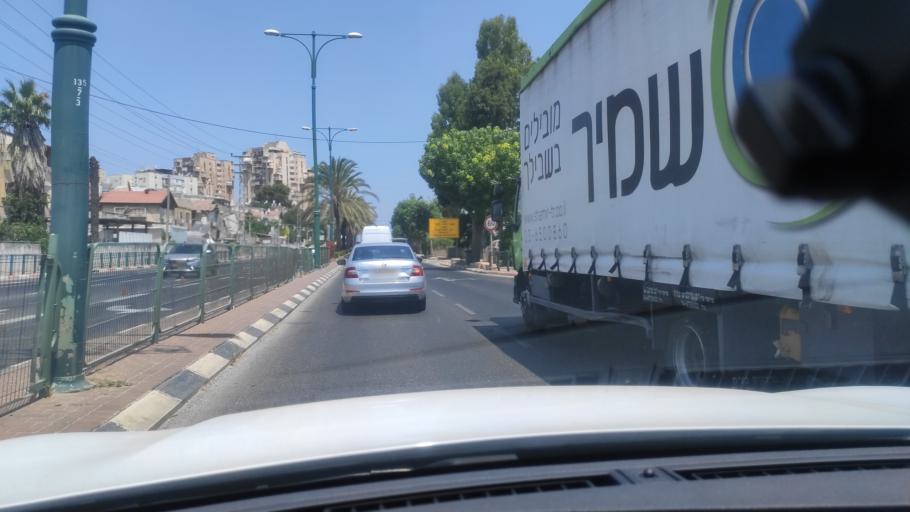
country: IL
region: Central District
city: Petah Tiqwa
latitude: 32.0974
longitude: 34.9012
